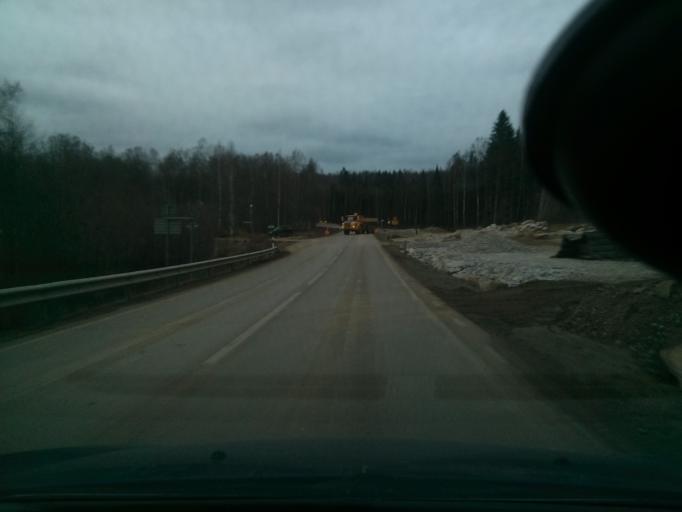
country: SE
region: Blekinge
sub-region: Ronneby Kommun
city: Brakne-Hoby
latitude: 56.3324
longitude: 15.1723
